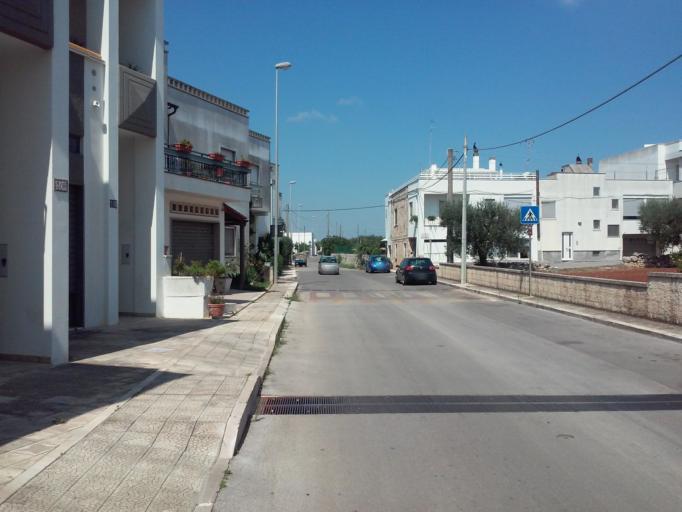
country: IT
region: Apulia
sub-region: Provincia di Bari
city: Alberobello
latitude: 40.7877
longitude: 17.2281
